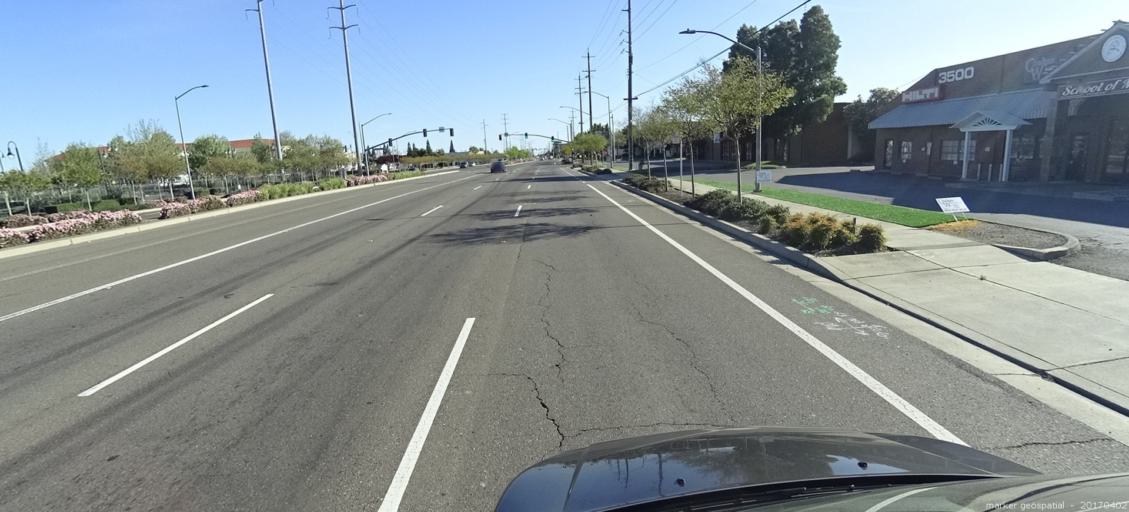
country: US
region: California
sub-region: Sacramento County
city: Rosemont
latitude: 38.5433
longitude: -121.4091
